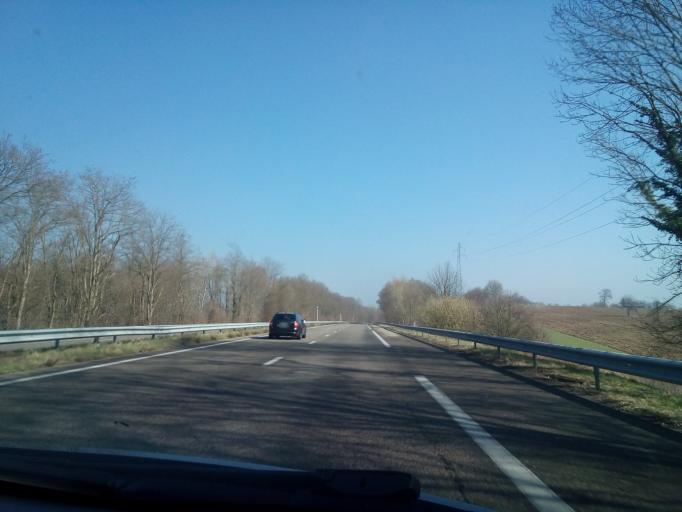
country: FR
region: Alsace
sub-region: Departement du Bas-Rhin
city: Seltz
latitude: 48.9333
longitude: 8.1246
